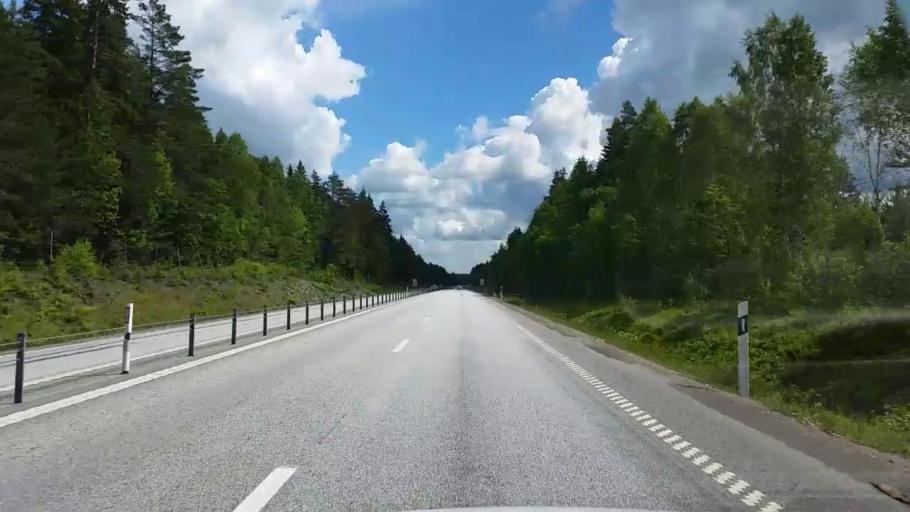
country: SE
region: Vaestmanland
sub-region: Norbergs Kommun
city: Norberg
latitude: 60.0572
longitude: 15.8673
